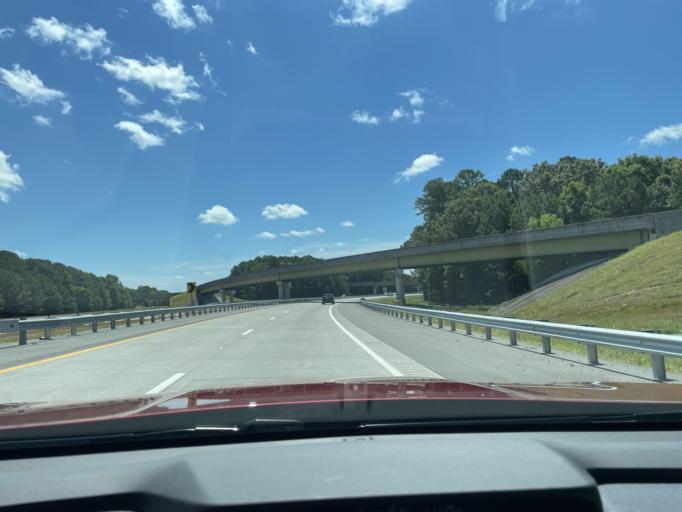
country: US
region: Arkansas
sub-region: Jefferson County
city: White Hall
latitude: 34.2451
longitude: -92.0936
